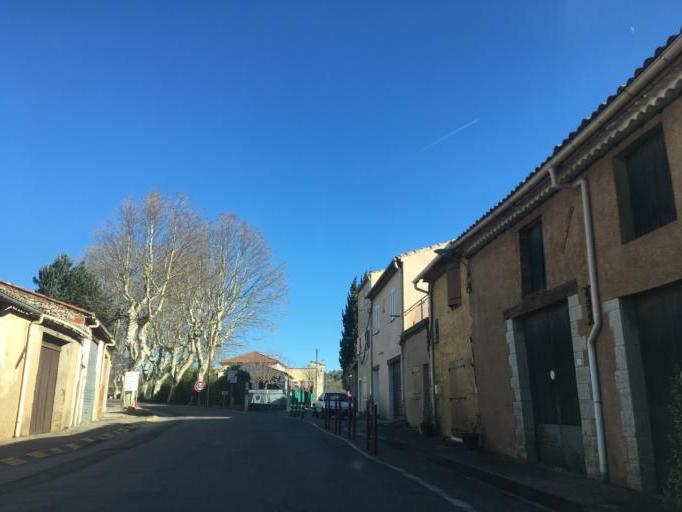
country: FR
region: Provence-Alpes-Cote d'Azur
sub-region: Departement du Var
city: Barjols
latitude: 43.5931
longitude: 6.0184
